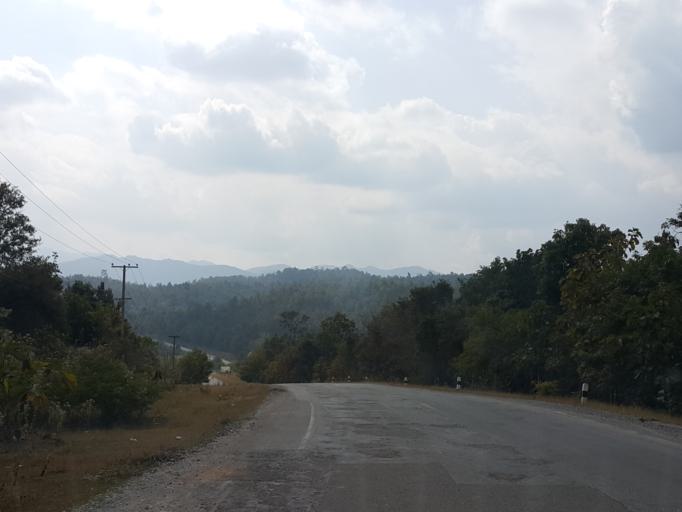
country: TH
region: Chiang Mai
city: Om Koi
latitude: 17.8298
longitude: 98.3648
